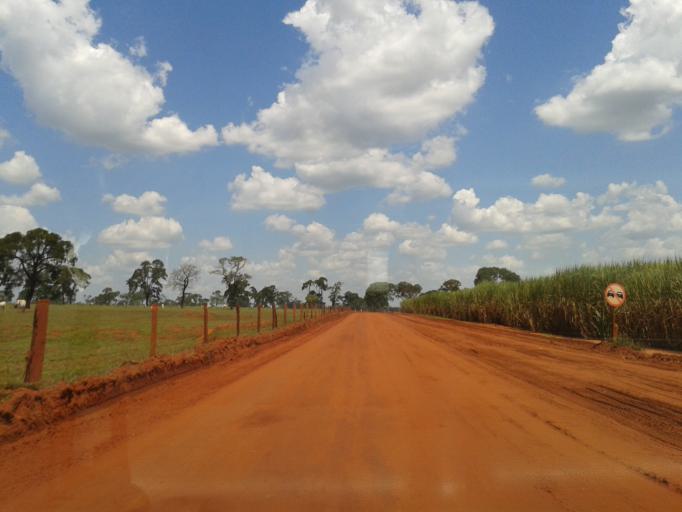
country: BR
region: Minas Gerais
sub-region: Ituiutaba
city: Ituiutaba
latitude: -18.9655
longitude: -49.6609
